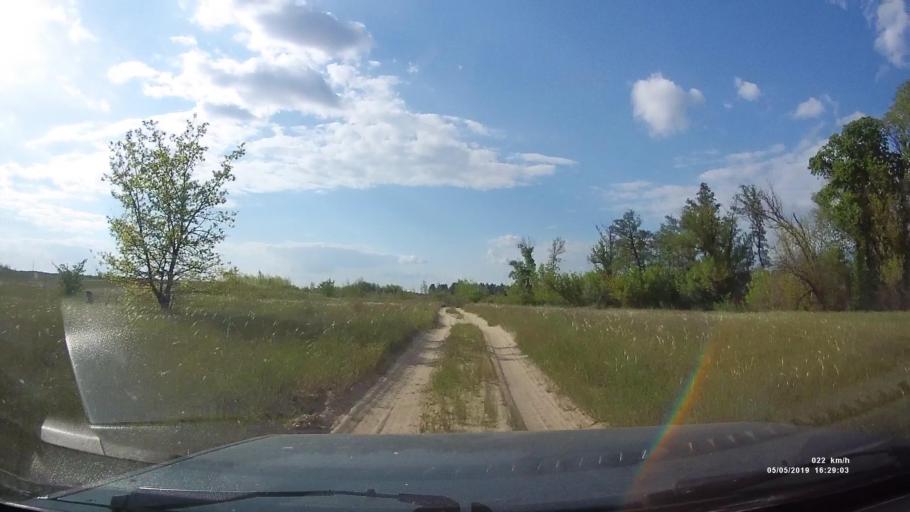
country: RU
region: Rostov
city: Ust'-Donetskiy
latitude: 47.7693
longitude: 41.0150
